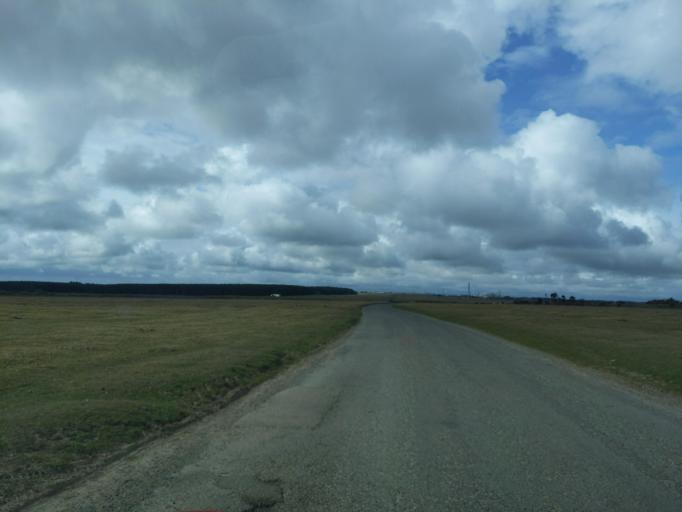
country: GB
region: England
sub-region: Cornwall
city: Camelford
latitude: 50.6285
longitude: -4.6001
